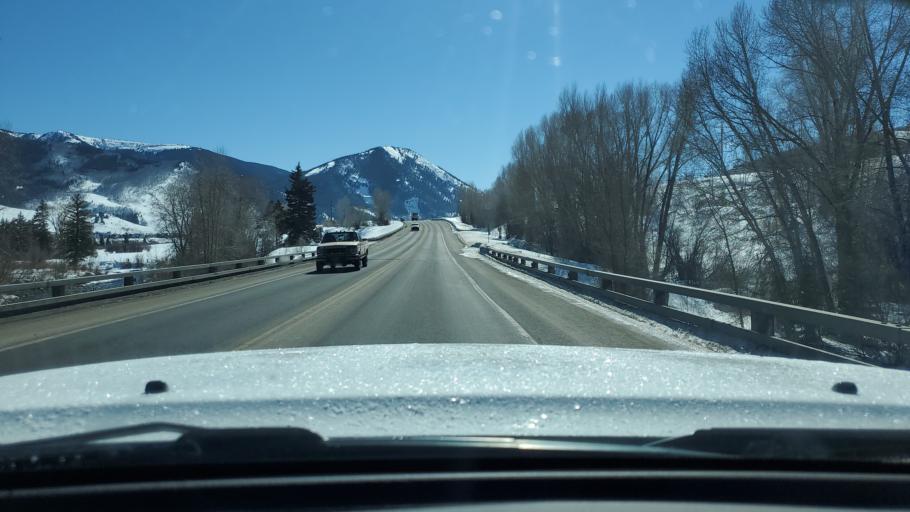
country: US
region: Colorado
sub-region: Gunnison County
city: Crested Butte
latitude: 38.8147
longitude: -106.9049
